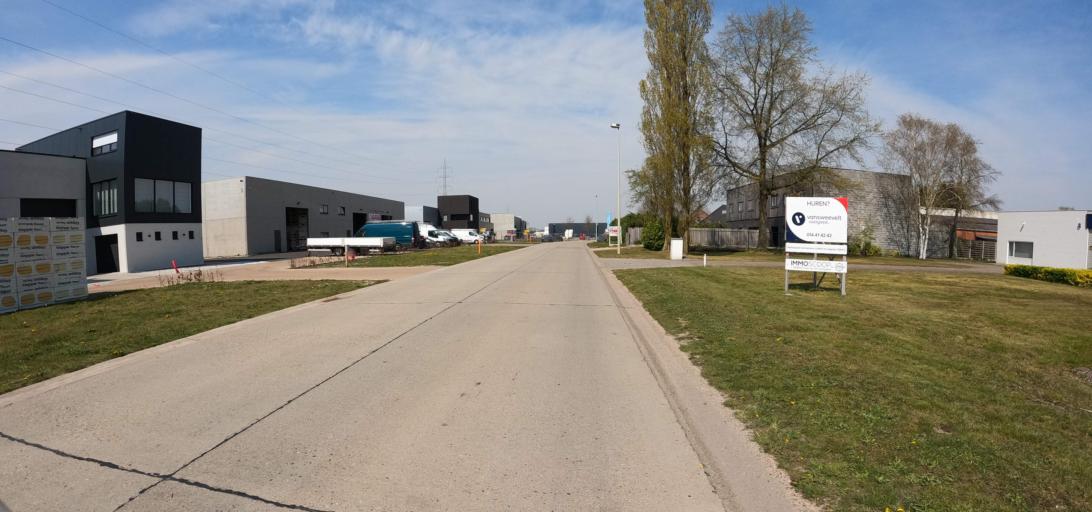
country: BE
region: Flanders
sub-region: Provincie Antwerpen
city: Beerse
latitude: 51.2989
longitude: 4.8307
